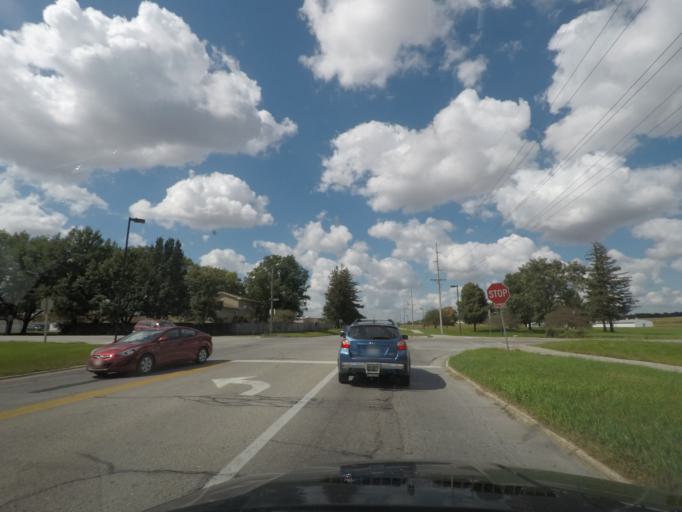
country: US
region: Iowa
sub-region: Story County
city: Ames
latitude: 42.0120
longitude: -93.6586
